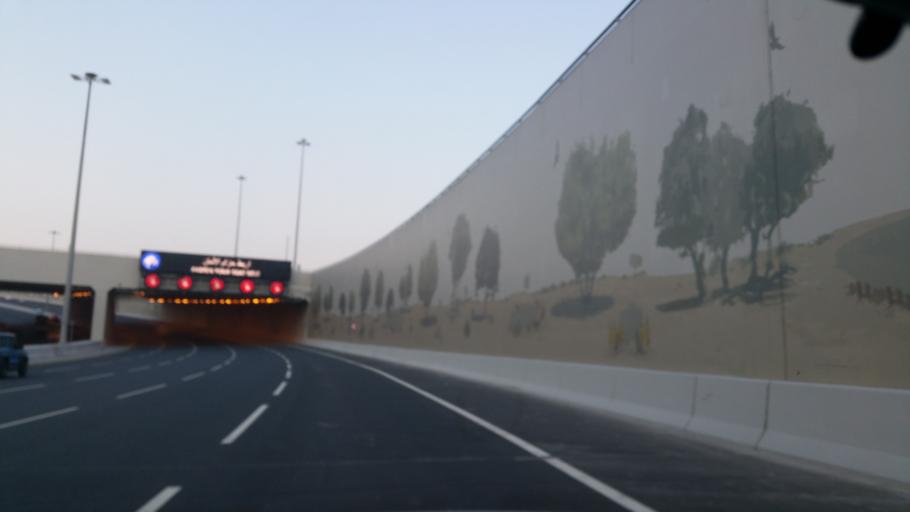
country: QA
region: Baladiyat ar Rayyan
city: Ar Rayyan
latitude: 25.3016
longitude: 51.4542
